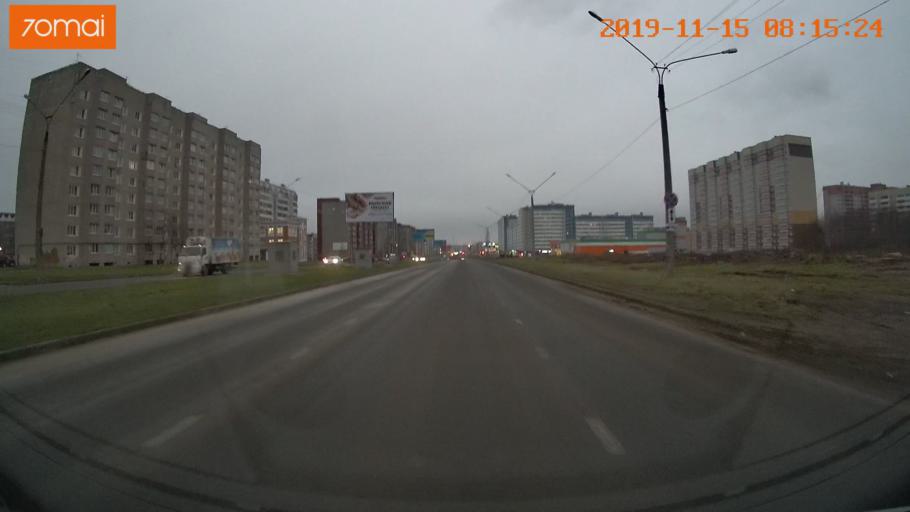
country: RU
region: Vologda
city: Cherepovets
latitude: 59.0820
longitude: 37.9226
